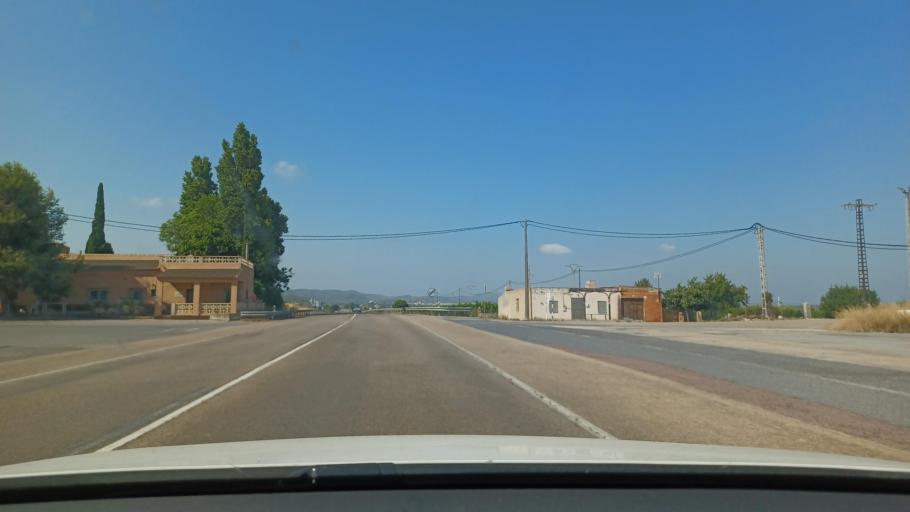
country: ES
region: Valencia
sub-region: Provincia de Castello
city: Torreblanca
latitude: 40.1640
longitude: 0.1644
